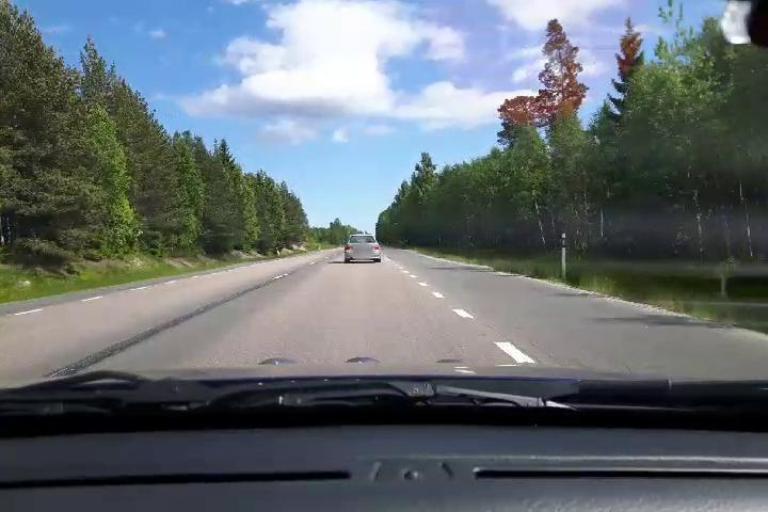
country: SE
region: Gaevleborg
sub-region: Hudiksvalls Kommun
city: Sorforsa
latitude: 61.7221
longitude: 17.0131
